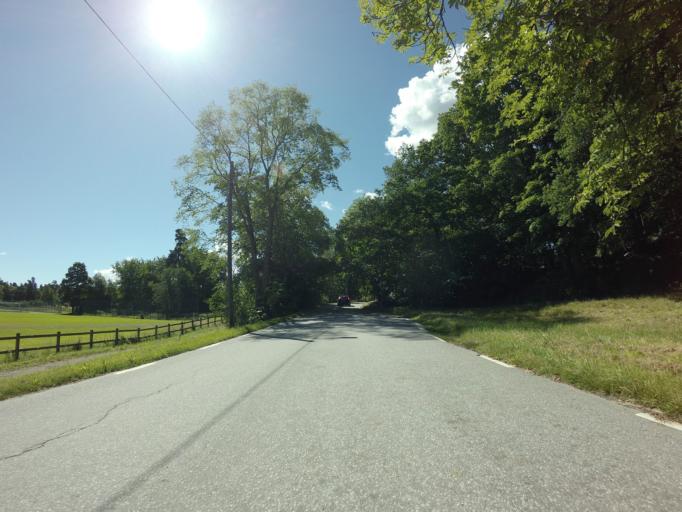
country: SE
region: Stockholm
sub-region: Lidingo
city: Lidingoe
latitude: 59.3345
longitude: 18.1338
